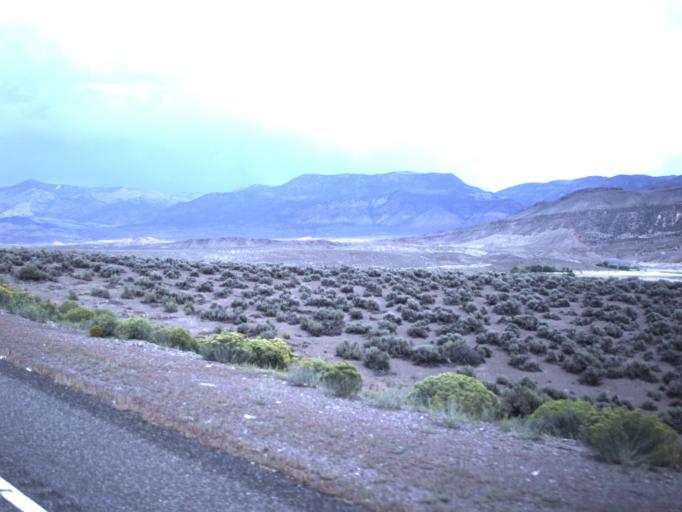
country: US
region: Utah
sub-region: Piute County
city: Junction
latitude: 38.3104
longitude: -112.2223
